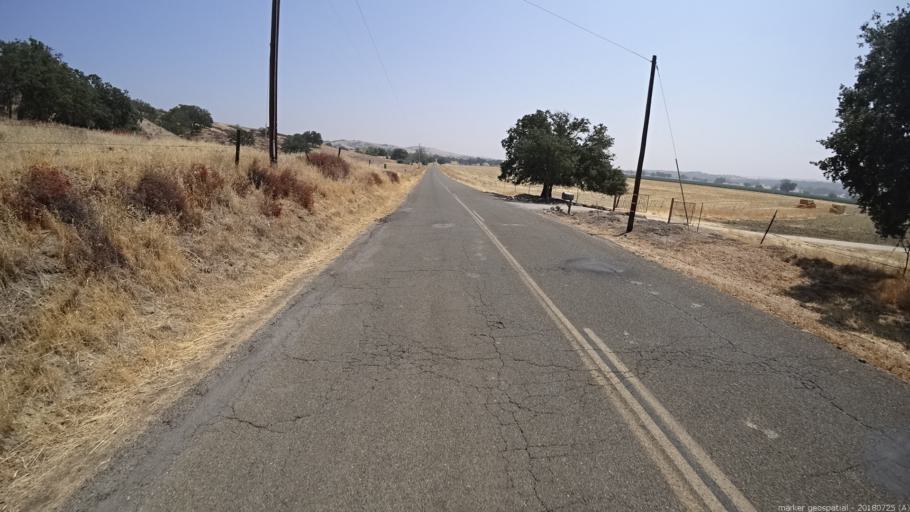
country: US
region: California
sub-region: Fresno County
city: Coalinga
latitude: 35.9031
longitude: -120.4497
